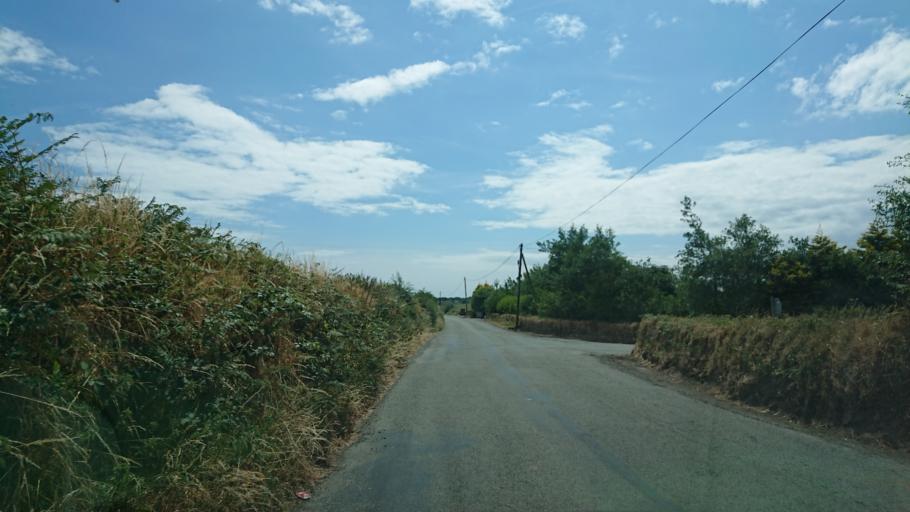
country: IE
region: Munster
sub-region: Waterford
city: Portlaw
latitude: 52.1886
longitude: -7.3326
